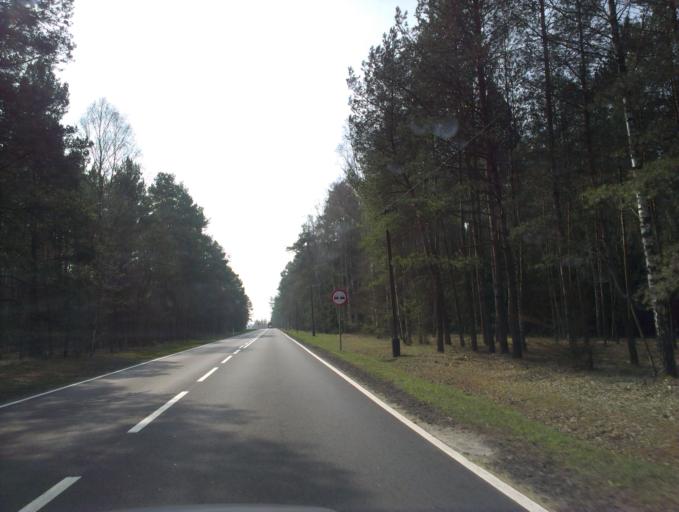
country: PL
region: Greater Poland Voivodeship
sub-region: Powiat zlotowski
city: Tarnowka
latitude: 53.2753
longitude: 16.7816
